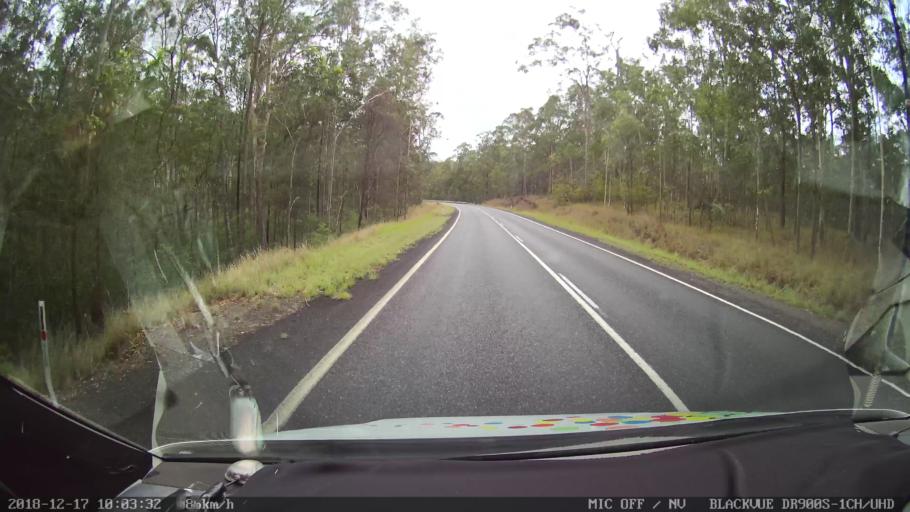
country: AU
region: New South Wales
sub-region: Tenterfield Municipality
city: Carrolls Creek
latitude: -28.8972
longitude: 152.4655
